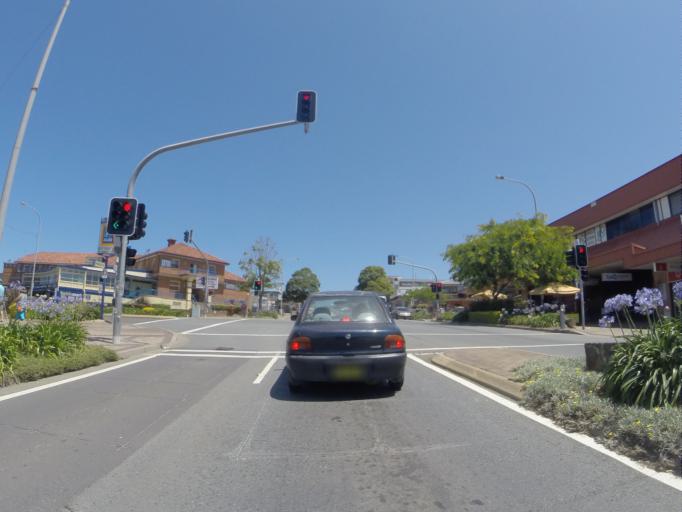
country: AU
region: New South Wales
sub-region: Shoalhaven Shire
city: Ulladulla
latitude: -35.3580
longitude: 150.4746
